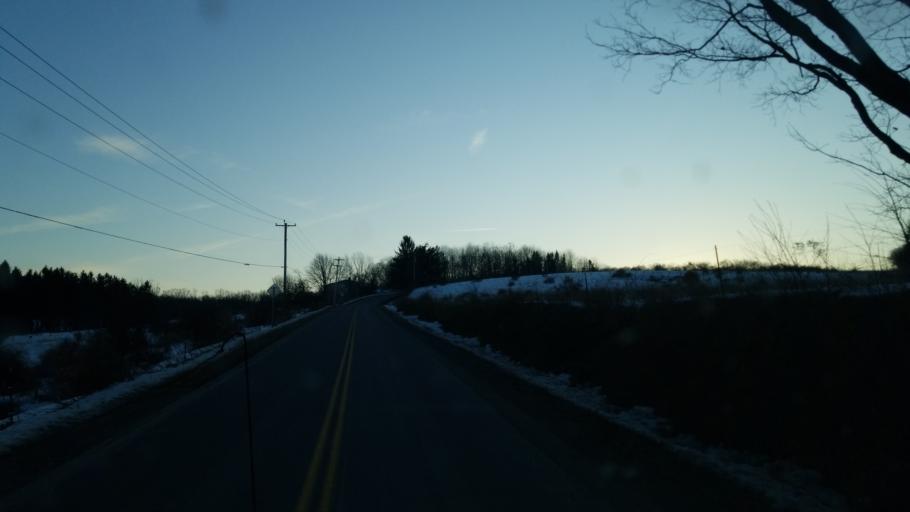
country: US
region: Pennsylvania
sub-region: Tioga County
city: Westfield
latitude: 42.0232
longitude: -77.6275
